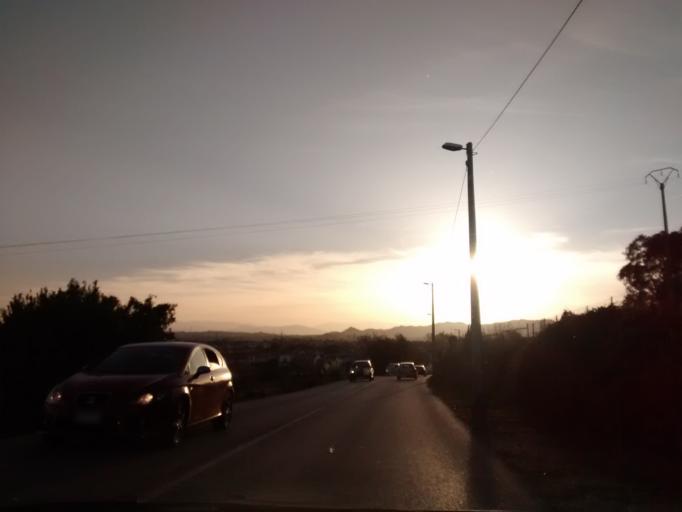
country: ES
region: Cantabria
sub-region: Provincia de Cantabria
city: Santa Cruz de Bezana
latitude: 43.4702
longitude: -3.8681
